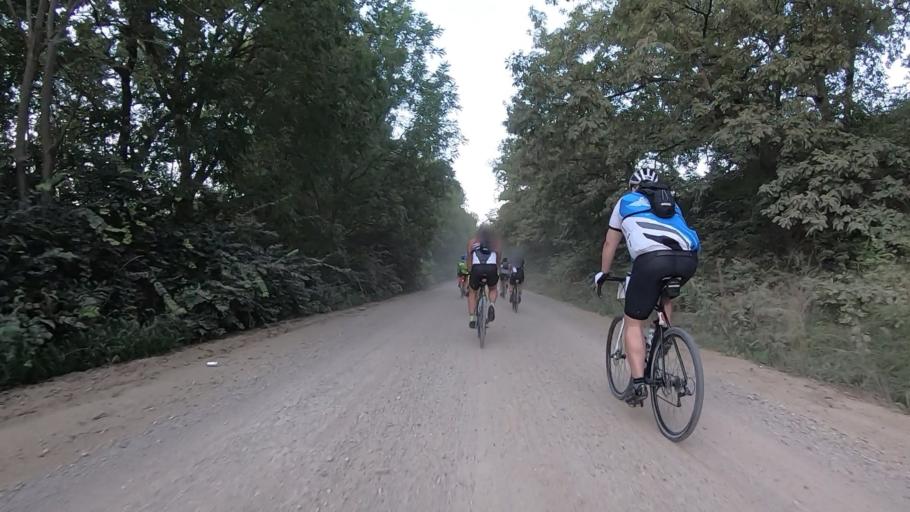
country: US
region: Kansas
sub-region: Marshall County
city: Marysville
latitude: 39.8410
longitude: -96.6643
